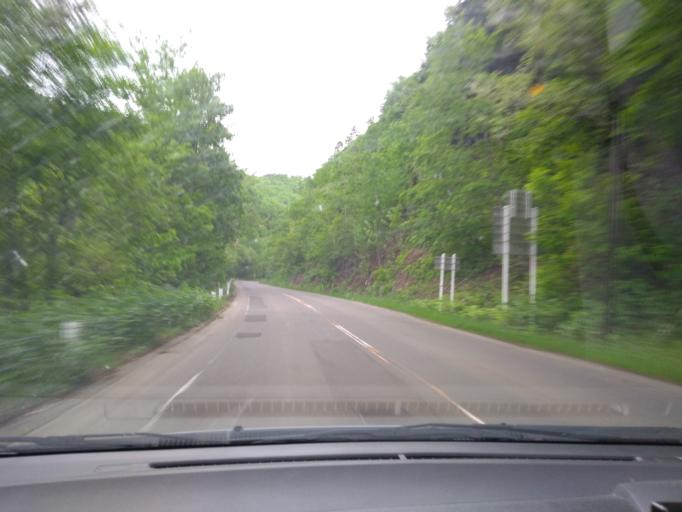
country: JP
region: Hokkaido
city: Shimo-furano
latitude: 43.1384
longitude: 142.4639
